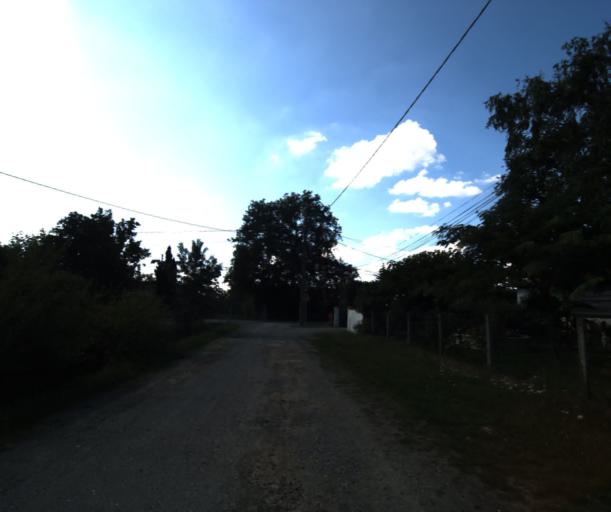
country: FR
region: Midi-Pyrenees
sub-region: Departement de la Haute-Garonne
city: Saint-Lys
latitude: 43.5009
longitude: 1.1923
